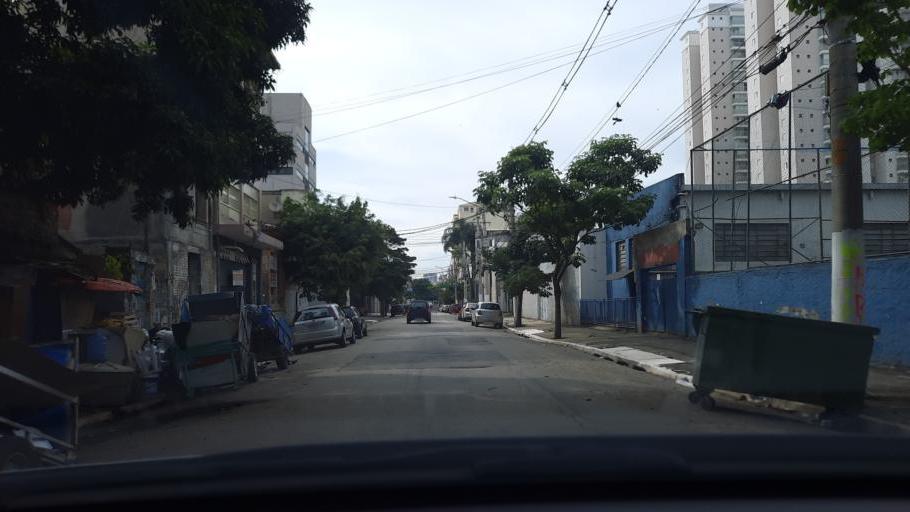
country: BR
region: Sao Paulo
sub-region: Sao Paulo
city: Sao Paulo
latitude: -23.5197
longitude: -46.6476
